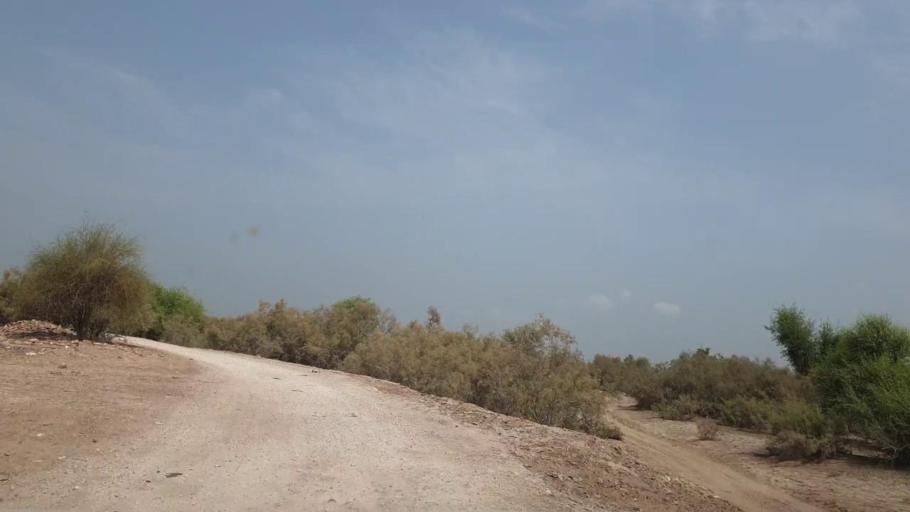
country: PK
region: Sindh
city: Dokri
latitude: 27.3966
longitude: 68.2591
